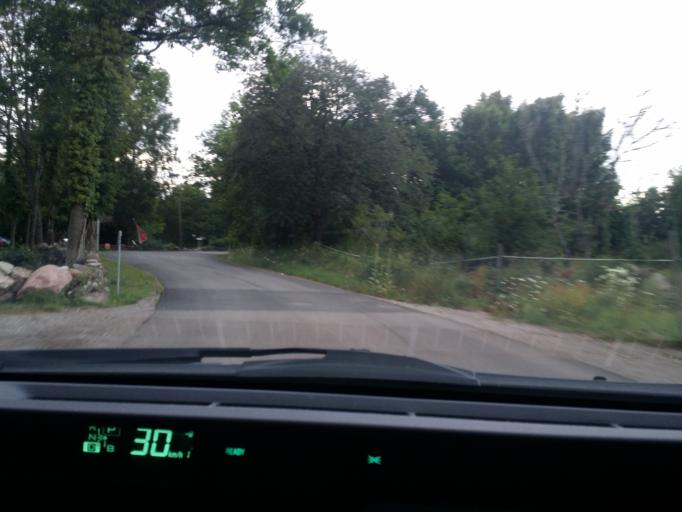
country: SE
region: Kalmar
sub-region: Borgholms Kommun
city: Borgholm
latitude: 57.2052
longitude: 16.9630
